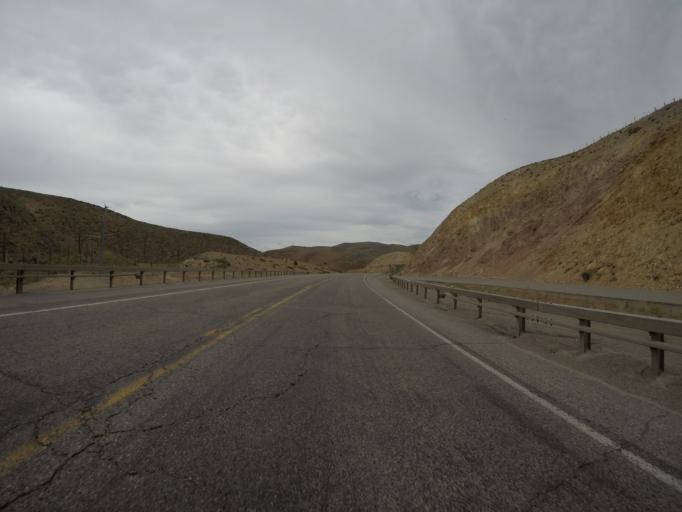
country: US
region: Wyoming
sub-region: Lincoln County
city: Kemmerer
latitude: 41.8204
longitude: -110.8081
